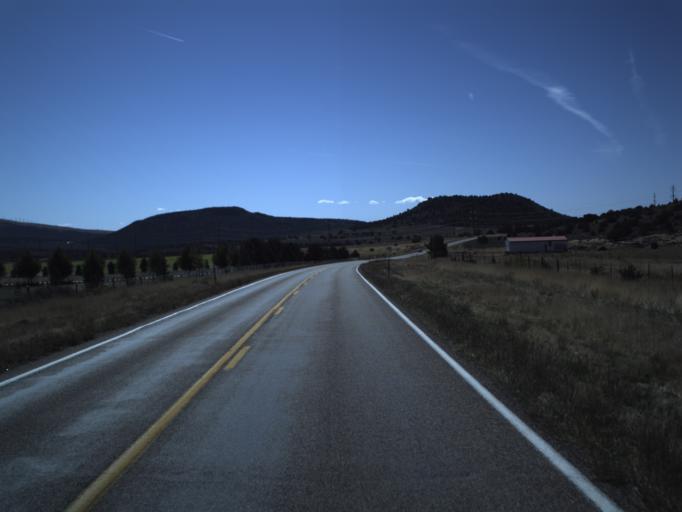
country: US
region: Utah
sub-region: Washington County
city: Enterprise
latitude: 37.4130
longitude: -113.6329
